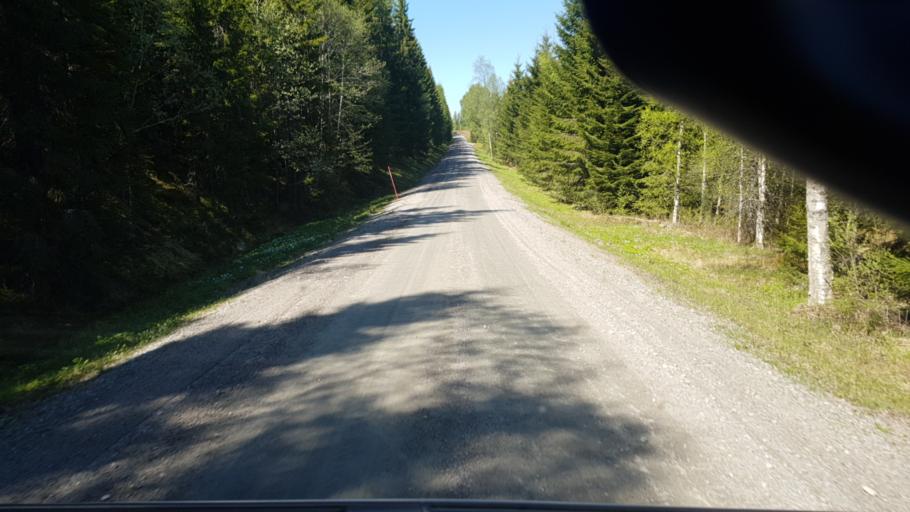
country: SE
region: Vaermland
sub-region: Arvika Kommun
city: Arvika
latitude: 59.8768
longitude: 12.6912
